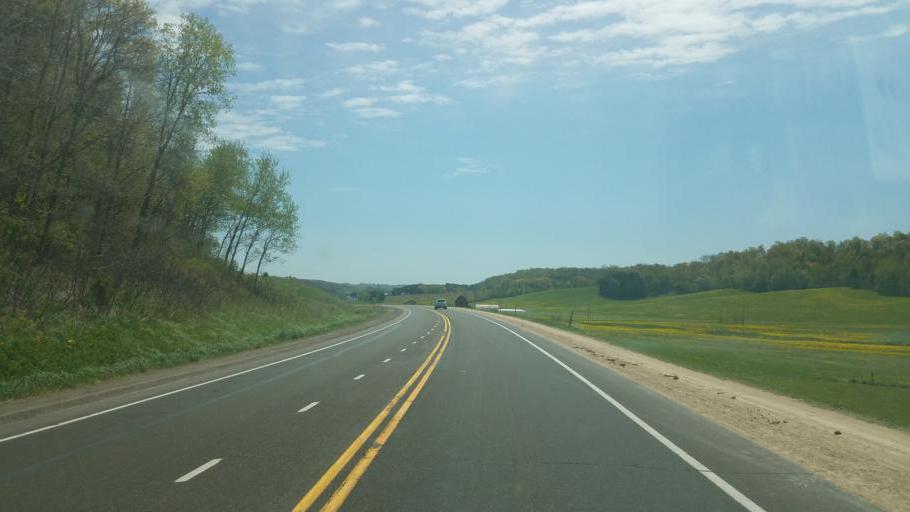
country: US
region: Wisconsin
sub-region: Monroe County
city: Tomah
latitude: 43.8786
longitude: -90.4812
